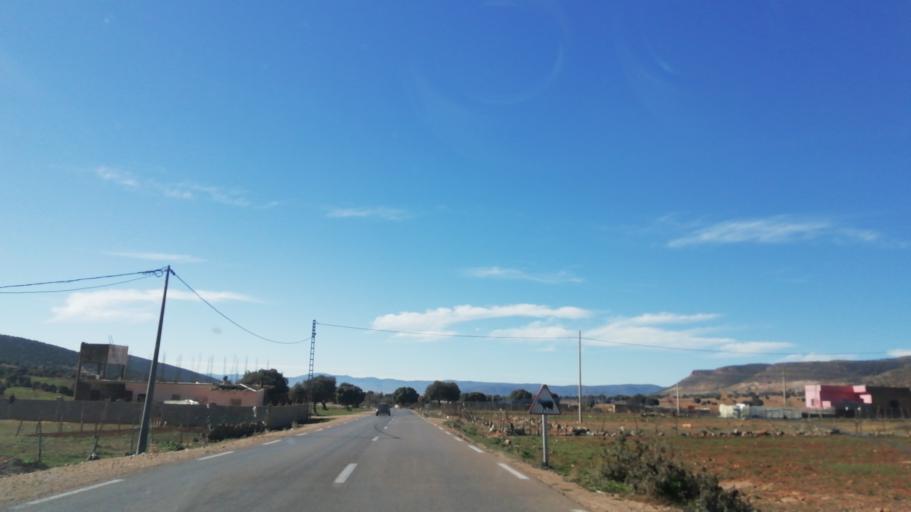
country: DZ
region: Tlemcen
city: Sebdou
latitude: 34.6977
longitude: -1.2333
